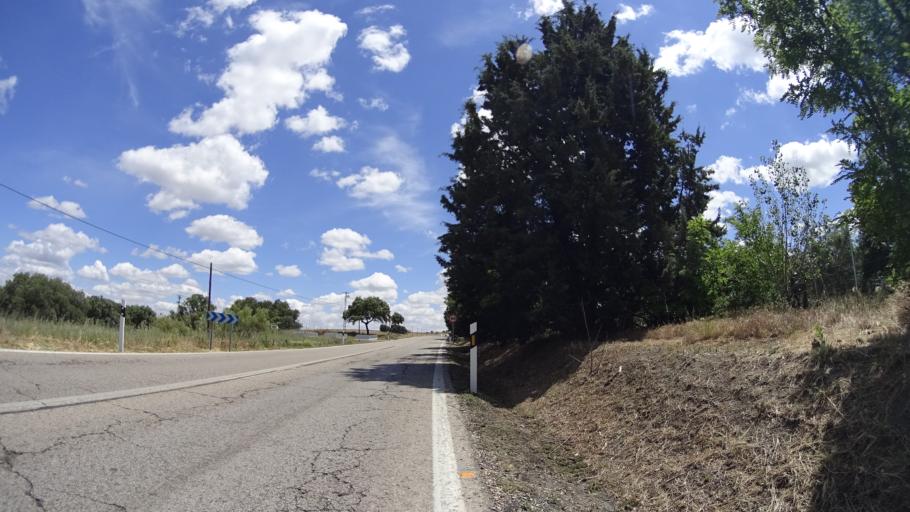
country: ES
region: Madrid
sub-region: Provincia de Madrid
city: Boadilla del Monte
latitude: 40.4150
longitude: -3.9381
